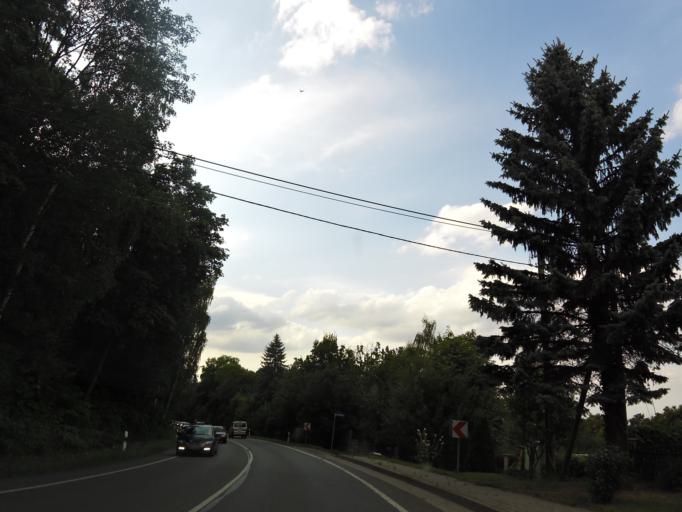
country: DE
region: Thuringia
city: Klettbach
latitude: 50.9337
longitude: 11.1290
